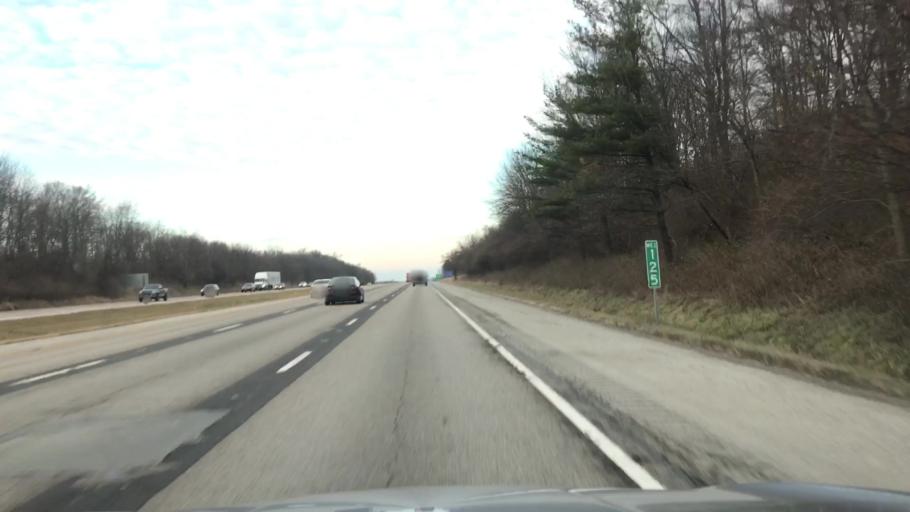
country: US
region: Illinois
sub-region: Logan County
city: Lincoln
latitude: 40.1473
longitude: -89.4171
